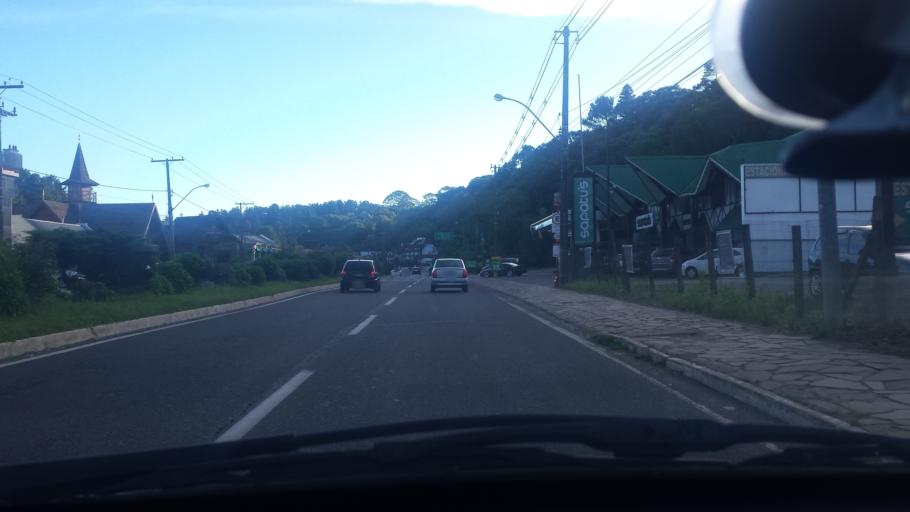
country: BR
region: Rio Grande do Sul
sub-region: Canela
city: Canela
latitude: -29.3702
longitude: -50.8624
